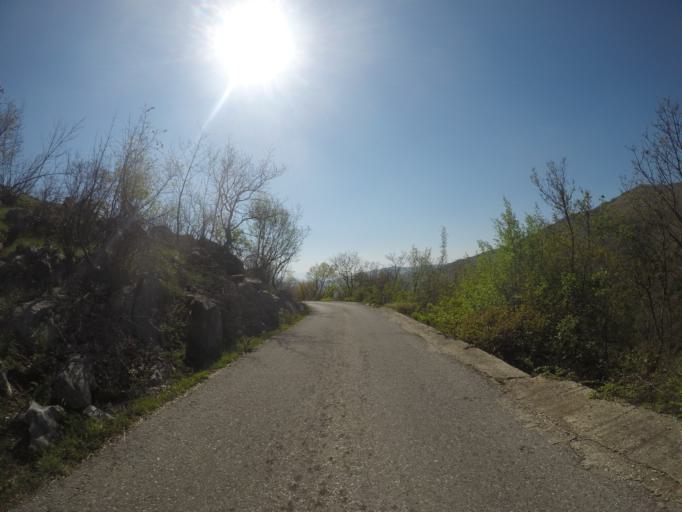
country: ME
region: Danilovgrad
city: Danilovgrad
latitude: 42.5160
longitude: 19.0662
